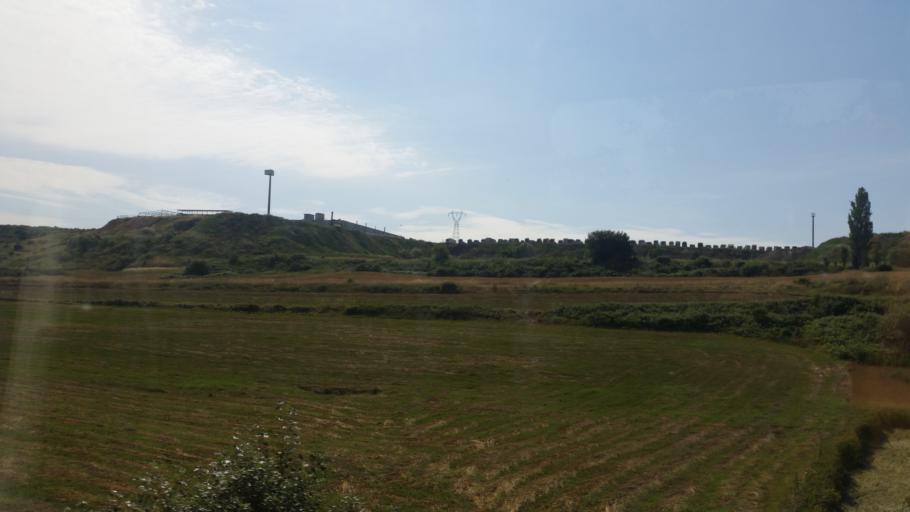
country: TR
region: Tekirdag
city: Corlu
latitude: 41.1962
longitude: 27.8168
